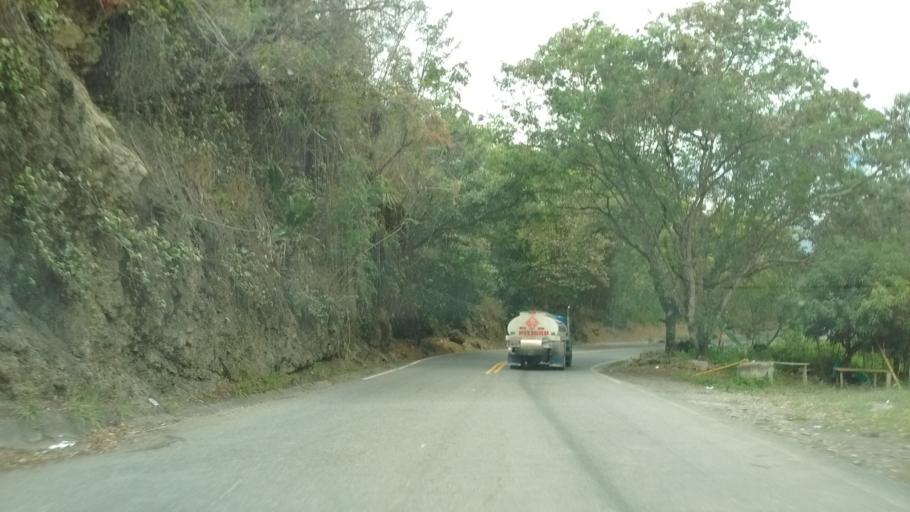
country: CO
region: Cauca
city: La Sierra
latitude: 2.1975
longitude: -76.8193
